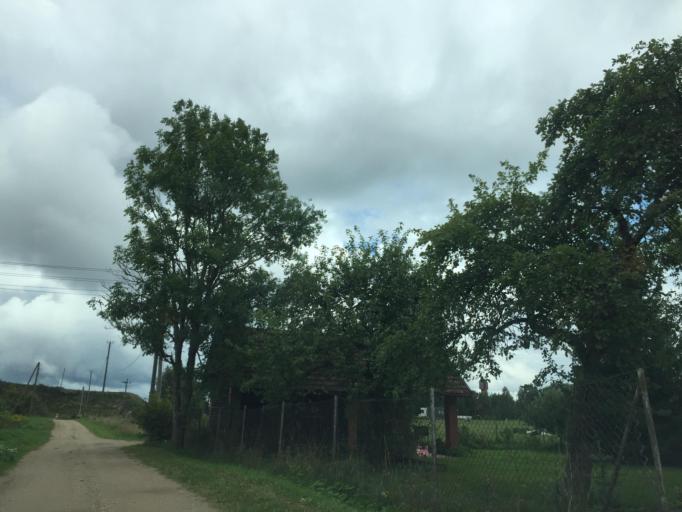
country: LV
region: Cesu Rajons
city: Cesis
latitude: 57.2950
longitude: 25.2278
